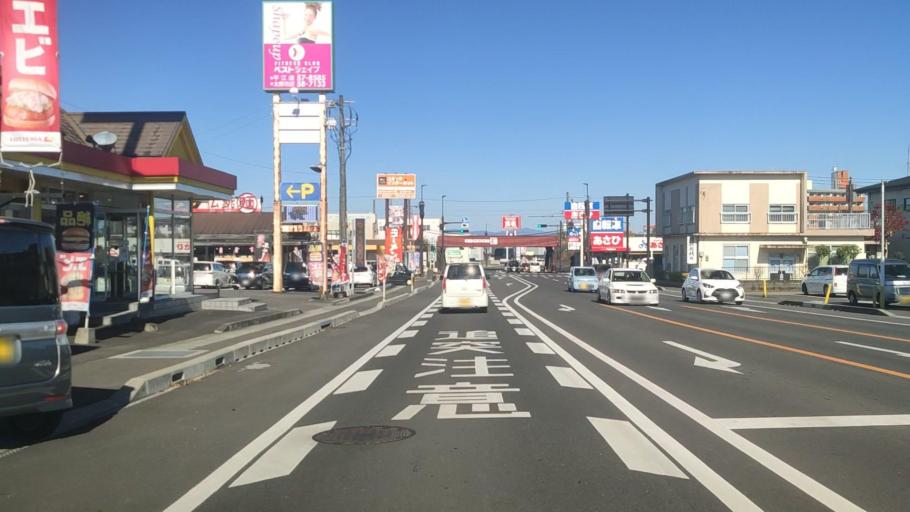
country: JP
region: Miyazaki
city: Miyakonojo
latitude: 31.7356
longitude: 131.0689
